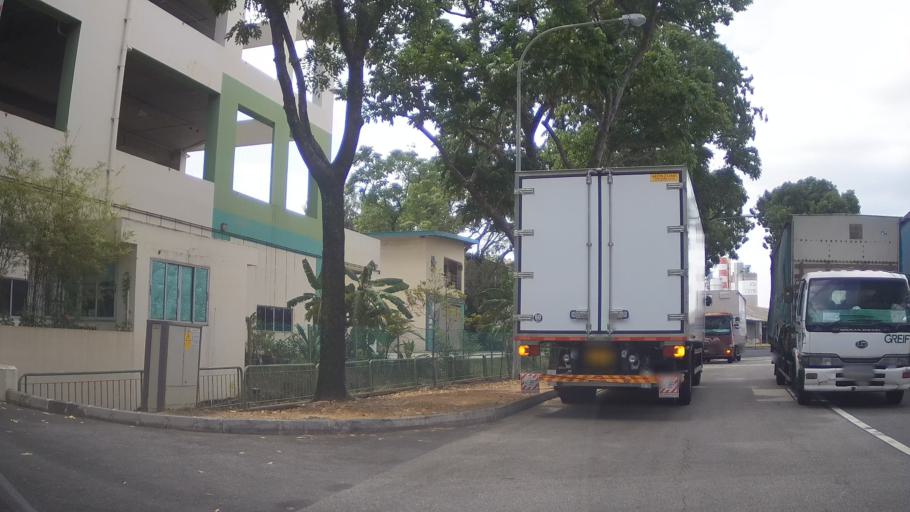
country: SG
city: Singapore
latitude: 1.3086
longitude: 103.7217
